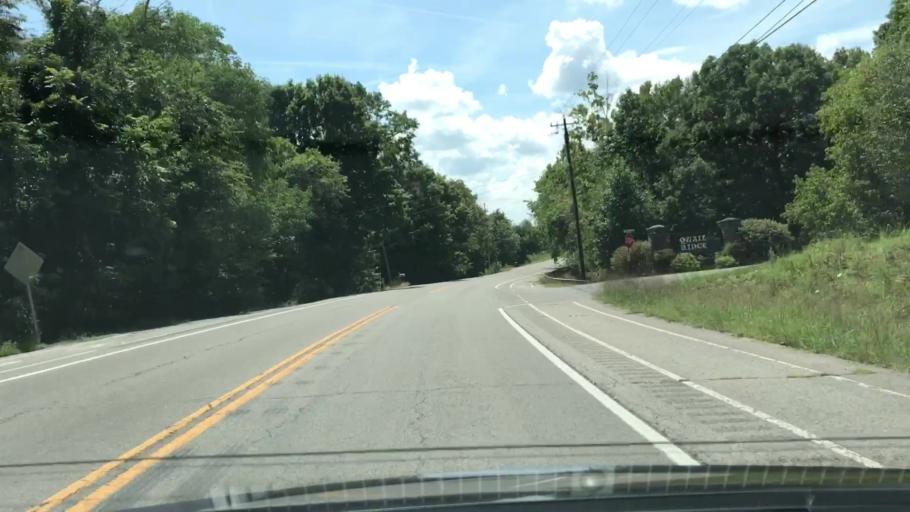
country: US
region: Tennessee
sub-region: Sumner County
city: White House
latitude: 36.4956
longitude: -86.6409
